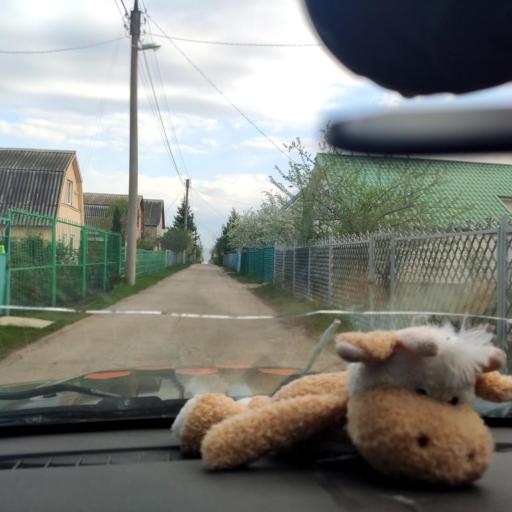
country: RU
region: Samara
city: Podstepki
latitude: 53.5094
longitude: 49.1889
